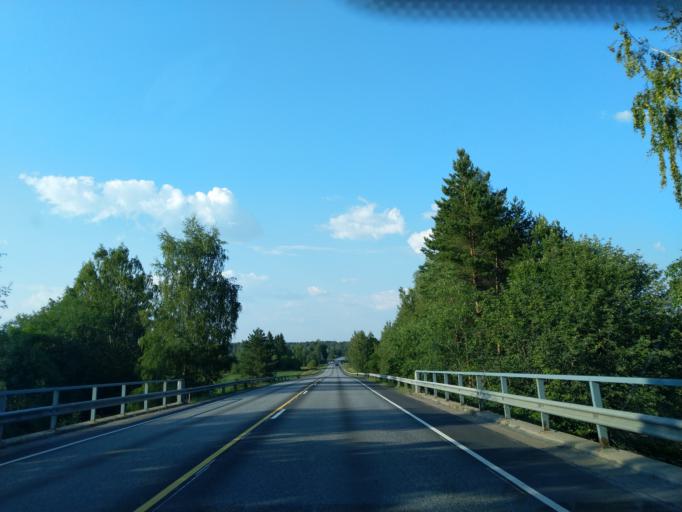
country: FI
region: Satakunta
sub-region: Pori
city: Pomarkku
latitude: 61.6922
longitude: 22.0012
